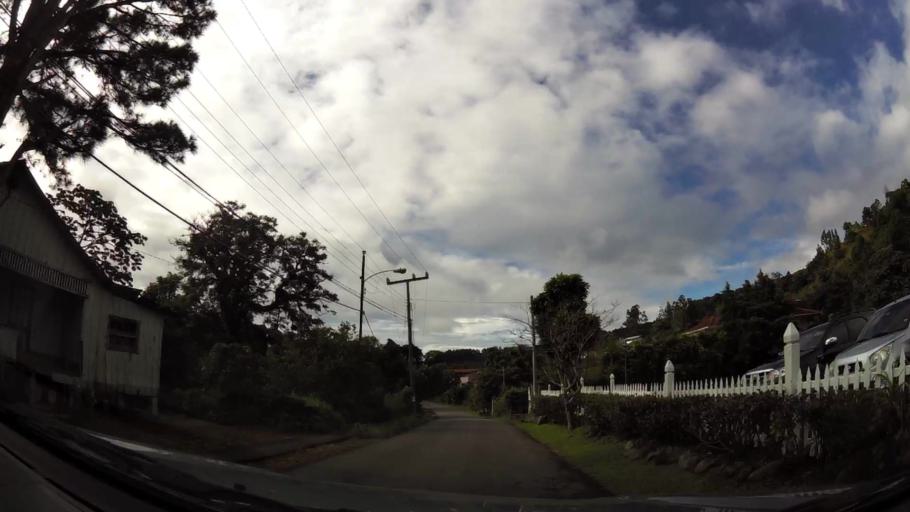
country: PA
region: Chiriqui
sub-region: Distrito Boquete
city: Boquete
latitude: 8.7825
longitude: -82.4320
